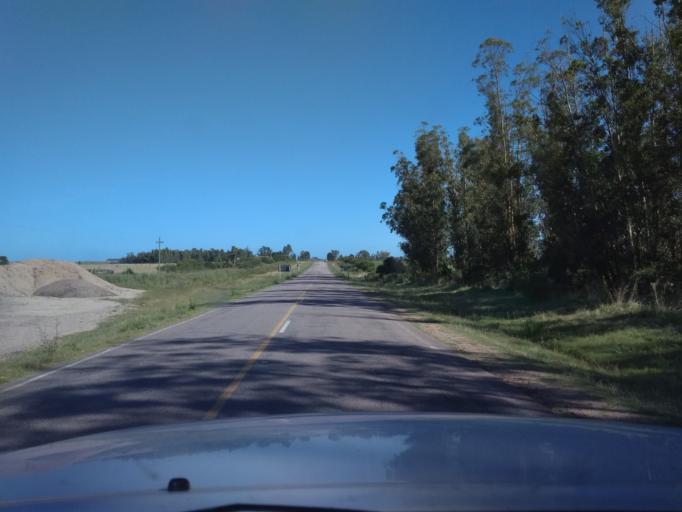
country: UY
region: Canelones
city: San Ramon
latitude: -34.2023
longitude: -55.9335
